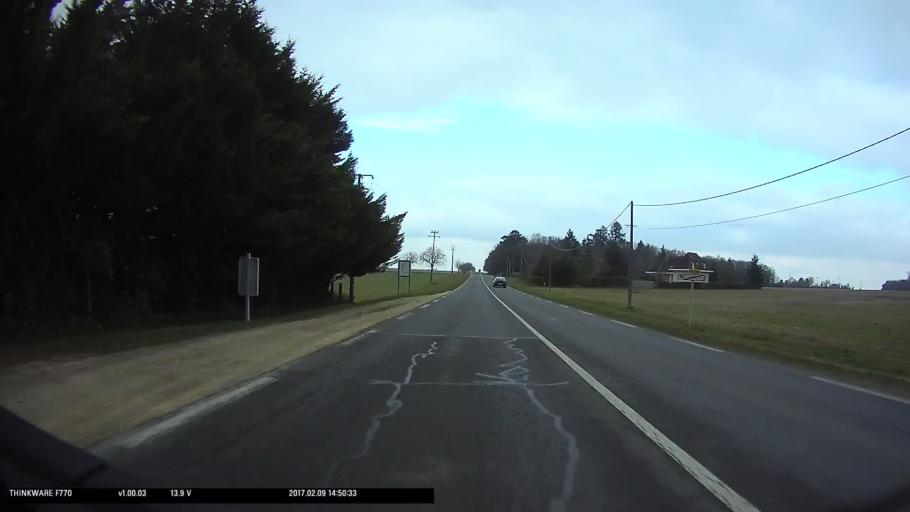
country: FR
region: Centre
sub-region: Departement du Cher
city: Levet
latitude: 46.9324
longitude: 2.4025
